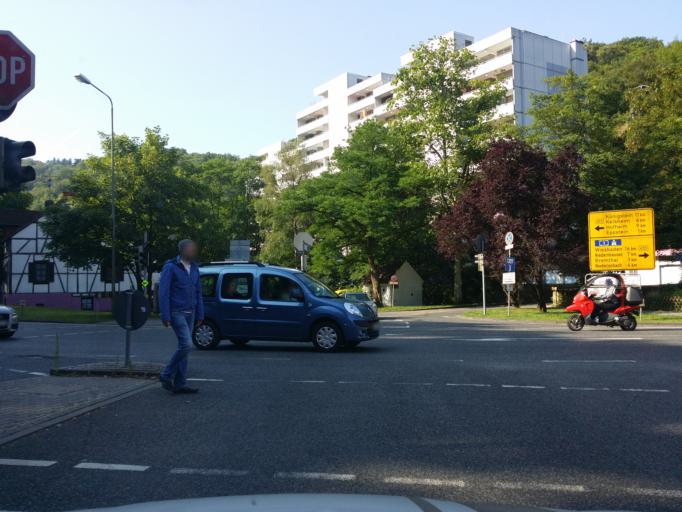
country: DE
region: Hesse
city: Eppstein
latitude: 50.1428
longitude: 8.3861
